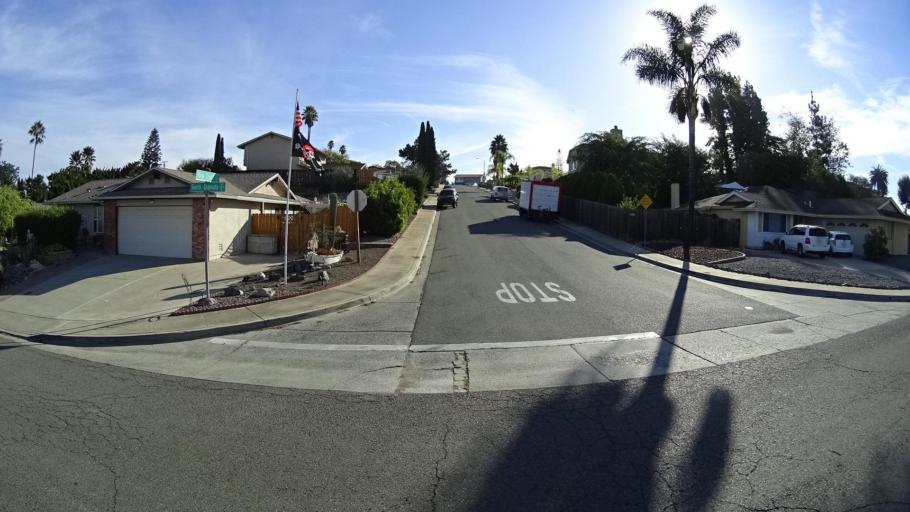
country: US
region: California
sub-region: San Diego County
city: Spring Valley
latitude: 32.7383
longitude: -116.9792
